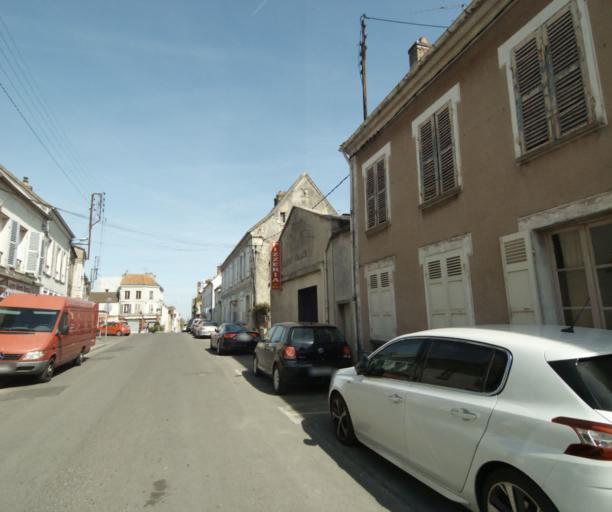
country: FR
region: Ile-de-France
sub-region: Departement de Seine-et-Marne
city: Nangis
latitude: 48.5556
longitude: 3.0138
